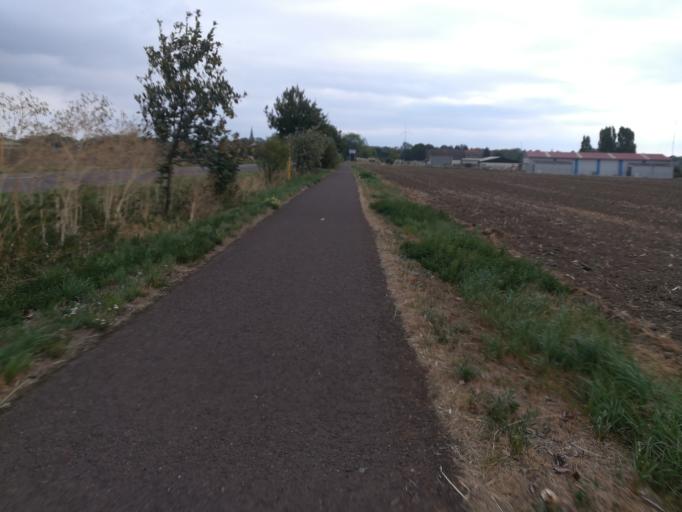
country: DE
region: Saxony-Anhalt
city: Irxleben
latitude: 52.1640
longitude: 11.4685
